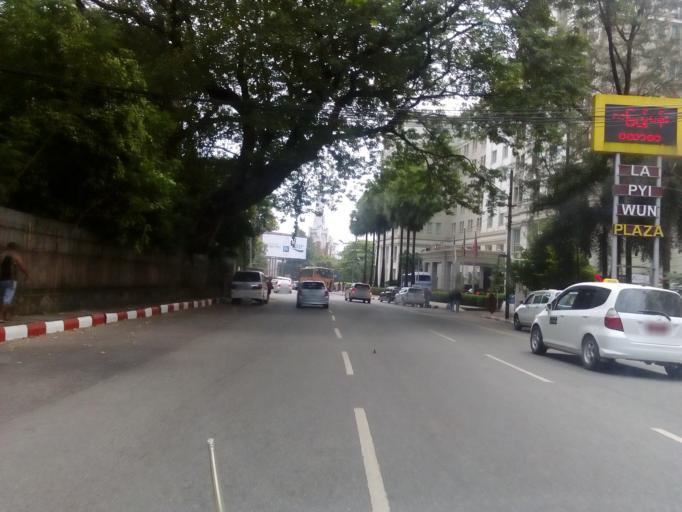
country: MM
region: Yangon
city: Yangon
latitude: 16.7841
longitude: 96.1580
